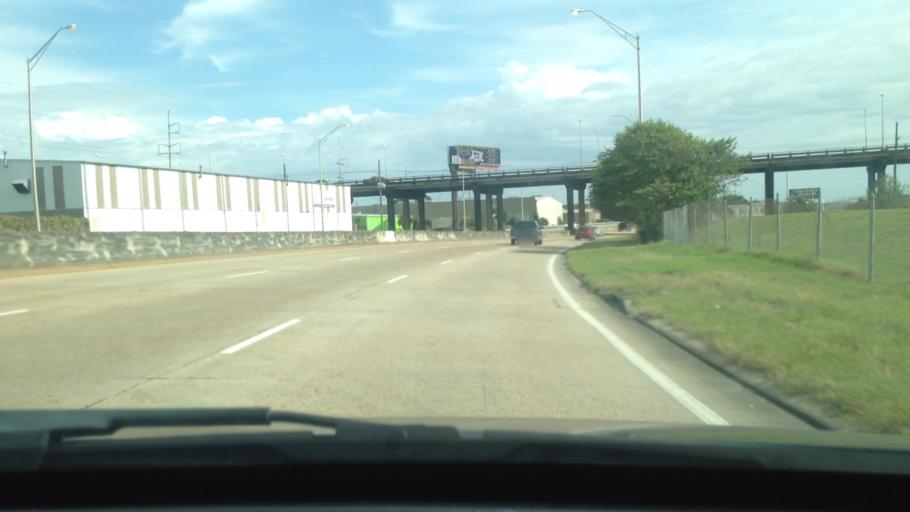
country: US
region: Louisiana
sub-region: Jefferson Parish
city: Jefferson
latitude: 29.9715
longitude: -90.1581
